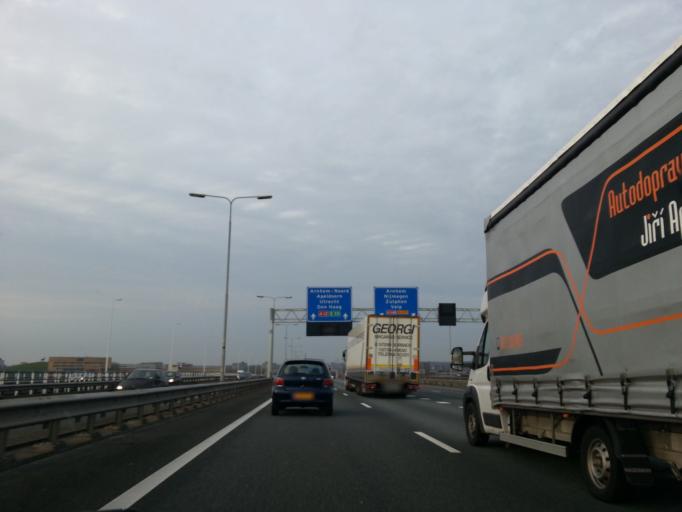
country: NL
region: Gelderland
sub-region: Gemeente Westervoort
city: Westervoort
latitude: 51.9742
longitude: 5.9902
